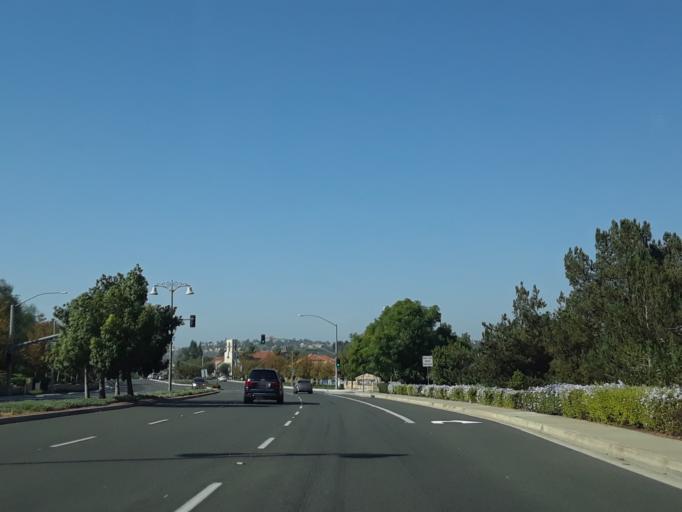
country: US
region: California
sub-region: Orange County
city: Mission Viejo
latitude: 33.5856
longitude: -117.6567
